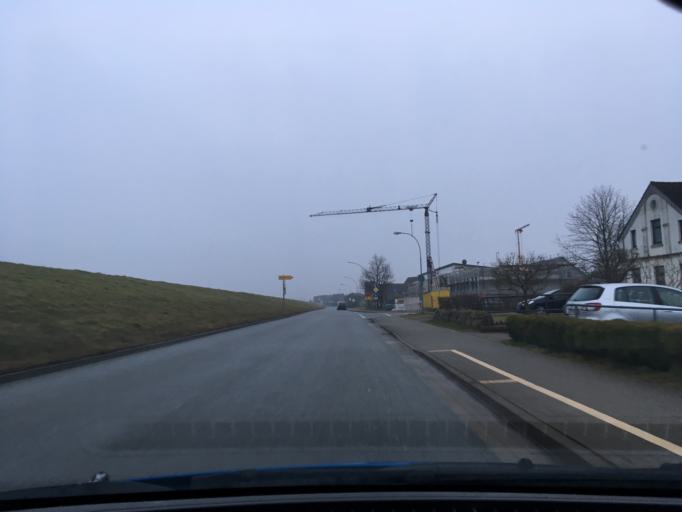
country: DE
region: Lower Saxony
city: Stelle
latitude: 53.4365
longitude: 10.0959
